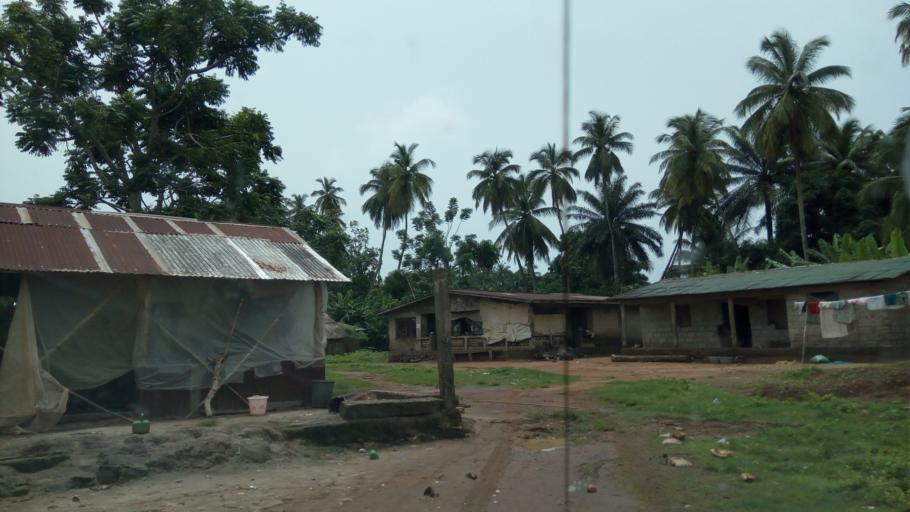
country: SL
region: Northern Province
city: Kassiri
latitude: 9.0456
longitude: -13.2693
